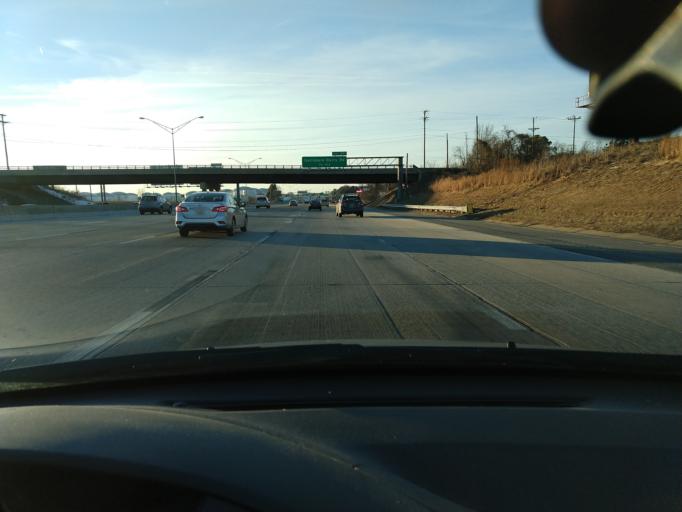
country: US
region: North Carolina
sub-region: Guilford County
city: Jamestown
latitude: 36.0703
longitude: -79.9281
